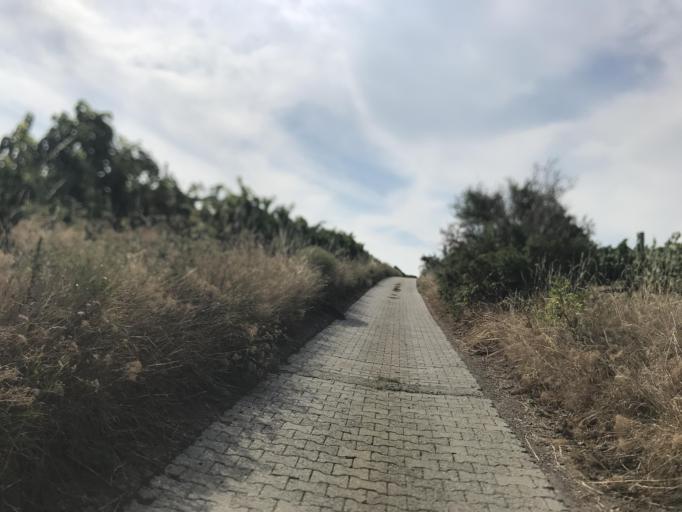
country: DE
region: Rheinland-Pfalz
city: Bechtolsheim
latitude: 49.7996
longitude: 8.1995
